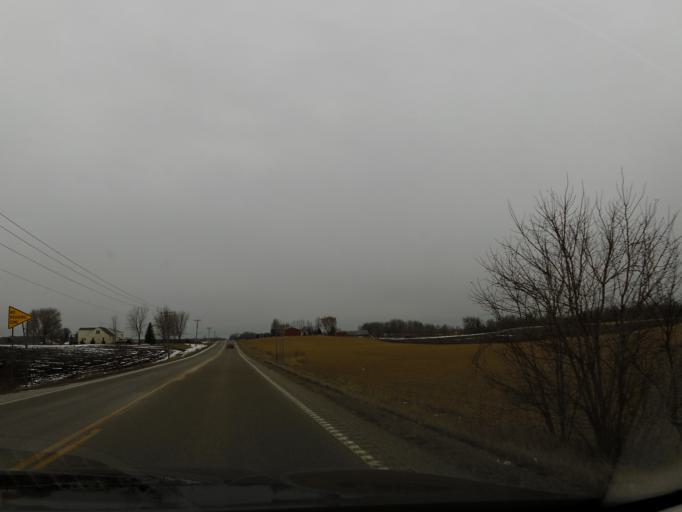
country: US
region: Minnesota
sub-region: Carver County
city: Waconia
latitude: 44.8110
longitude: -93.7882
